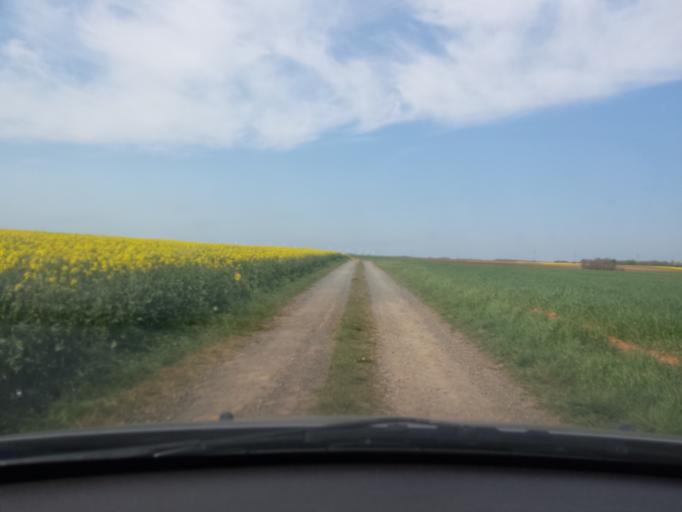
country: FR
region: Pays de la Loire
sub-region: Departement de la Vendee
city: Sainte-Gemme-la-Plaine
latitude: 46.4893
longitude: -1.0785
